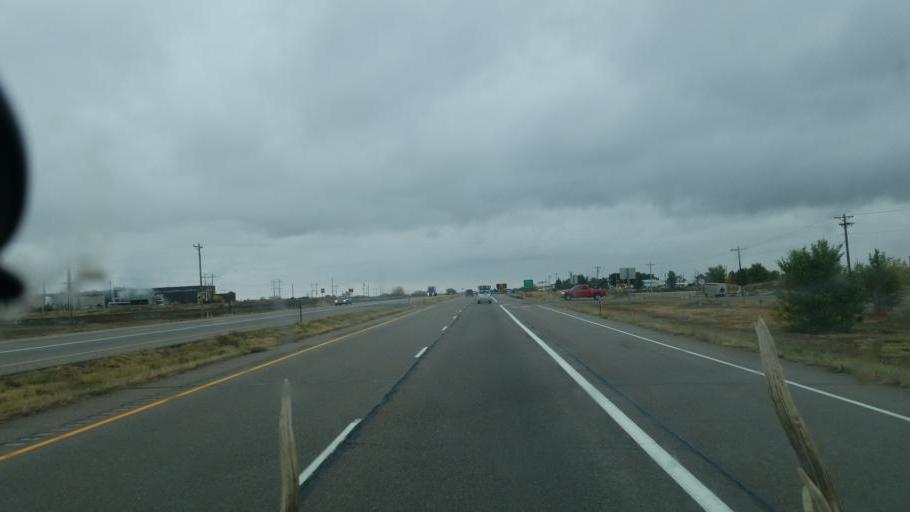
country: US
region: Colorado
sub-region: Pueblo County
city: Pueblo
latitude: 38.2745
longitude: -104.5212
